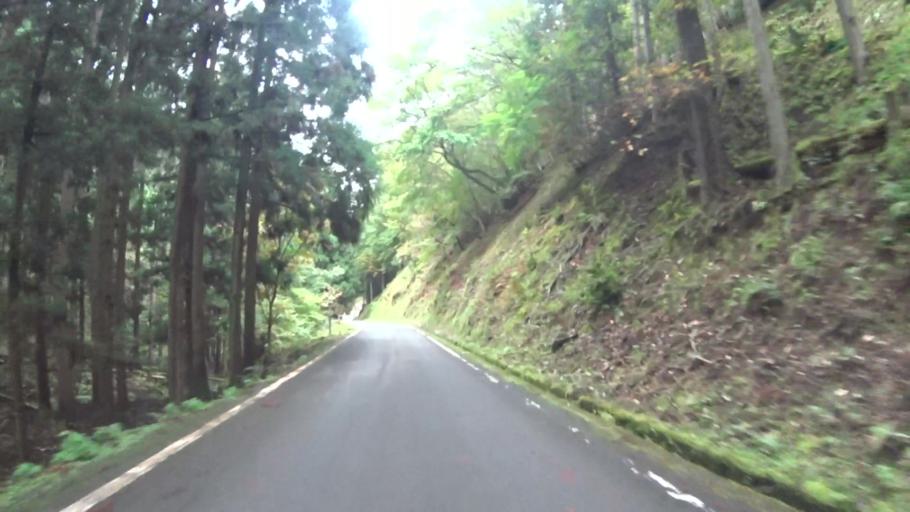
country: JP
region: Fukui
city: Obama
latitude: 35.2750
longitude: 135.7042
